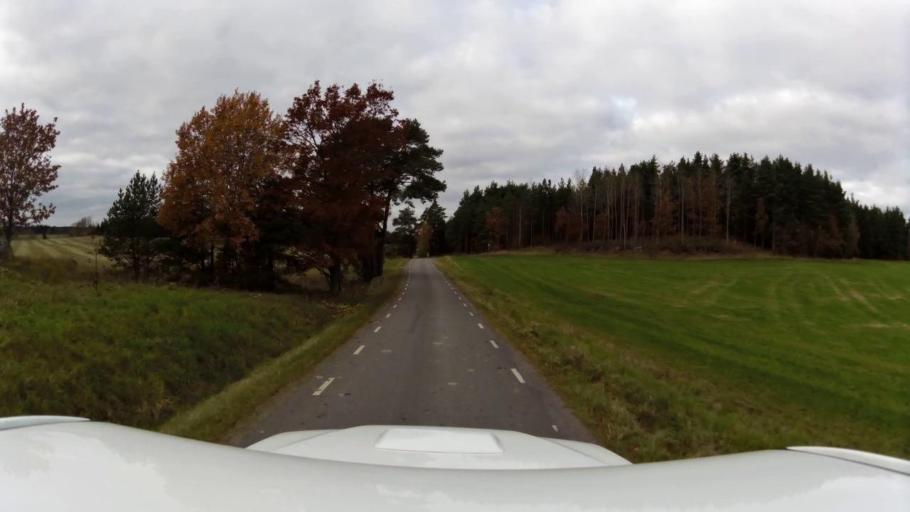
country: SE
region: OEstergoetland
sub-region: Linkopings Kommun
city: Linghem
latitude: 58.3920
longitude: 15.8057
